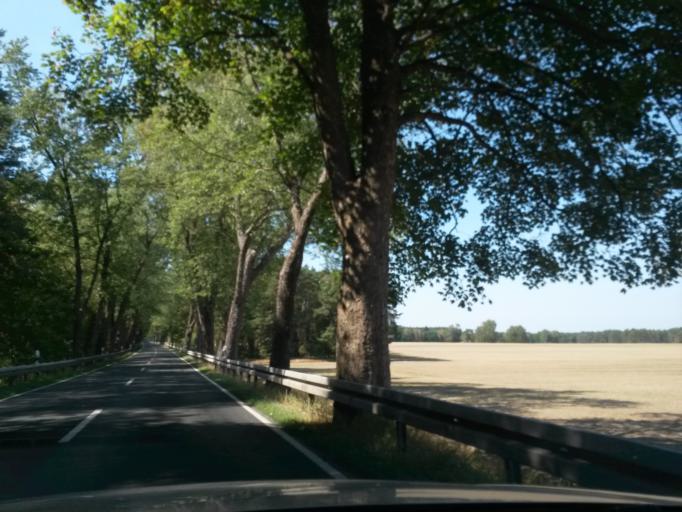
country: DE
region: Brandenburg
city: Wiesenburg
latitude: 52.1677
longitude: 12.4512
